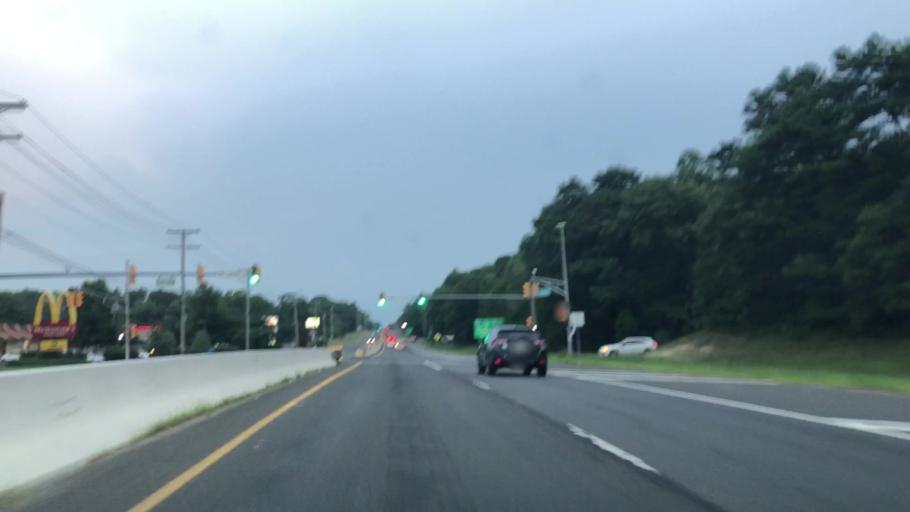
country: US
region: New Jersey
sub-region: Monmouth County
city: Shrewsbury
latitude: 40.1570
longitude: -74.4286
